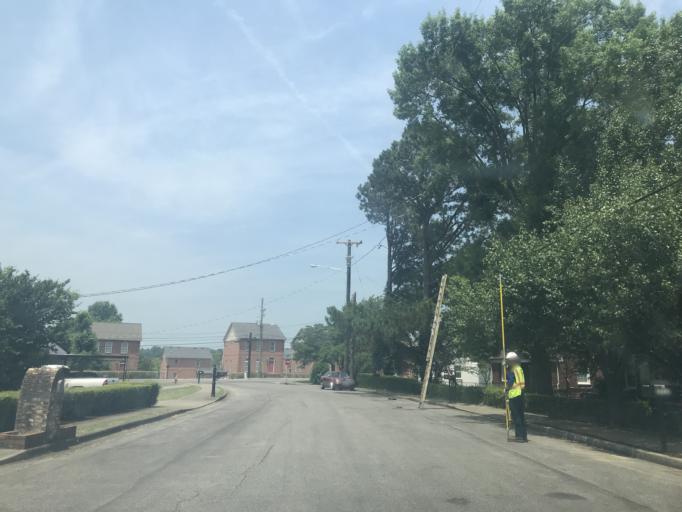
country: US
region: Tennessee
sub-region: Davidson County
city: Nashville
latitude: 36.1840
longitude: -86.8220
